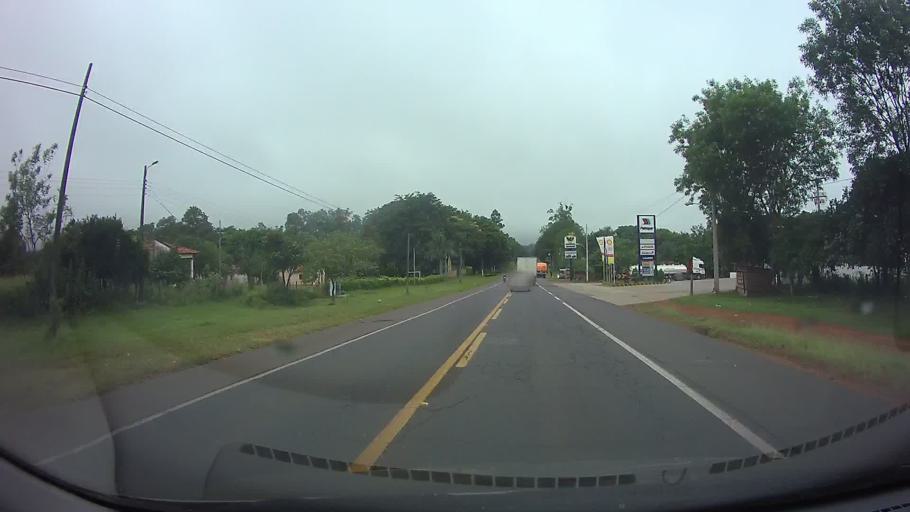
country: PY
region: Paraguari
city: Paraguari
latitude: -25.6001
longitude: -57.1990
